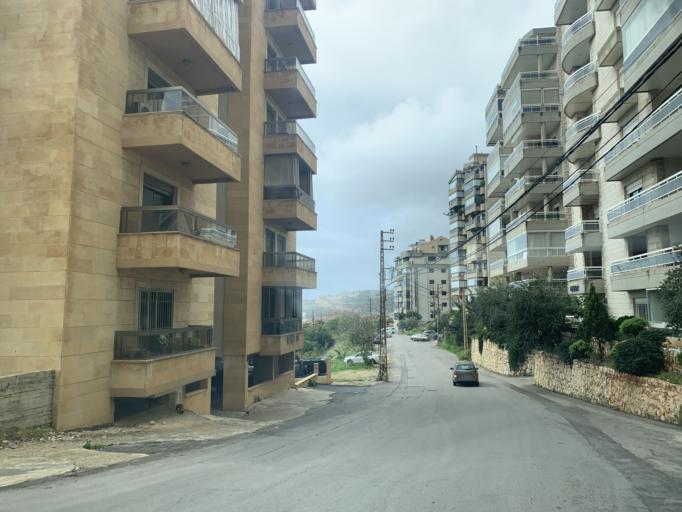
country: LB
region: Mont-Liban
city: Djounie
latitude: 34.0026
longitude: 35.6517
